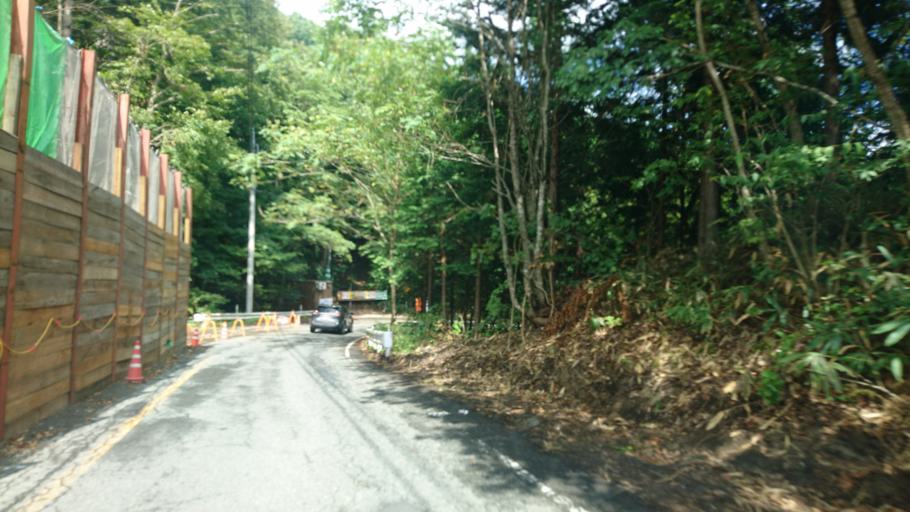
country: JP
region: Gunma
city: Omamacho-omama
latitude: 36.5987
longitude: 139.2354
